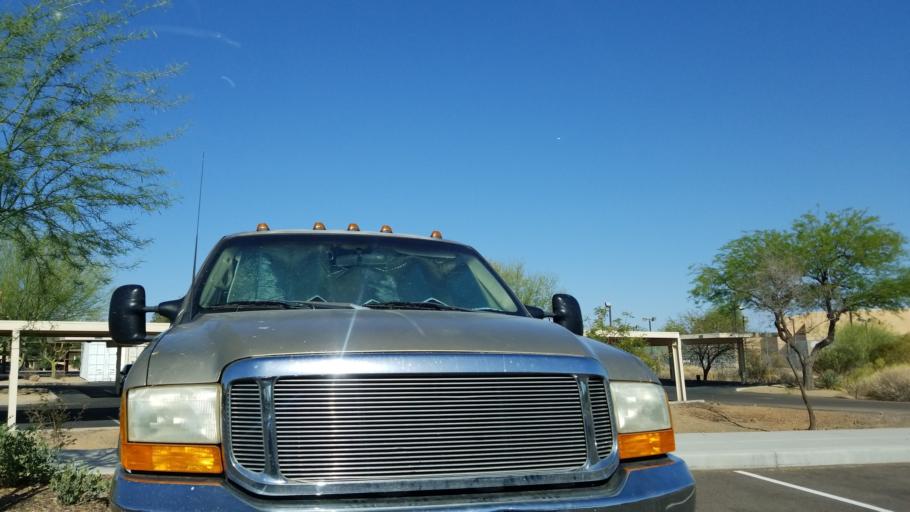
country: US
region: Arizona
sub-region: Maricopa County
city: Scottsdale
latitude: 33.5803
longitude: -111.8790
